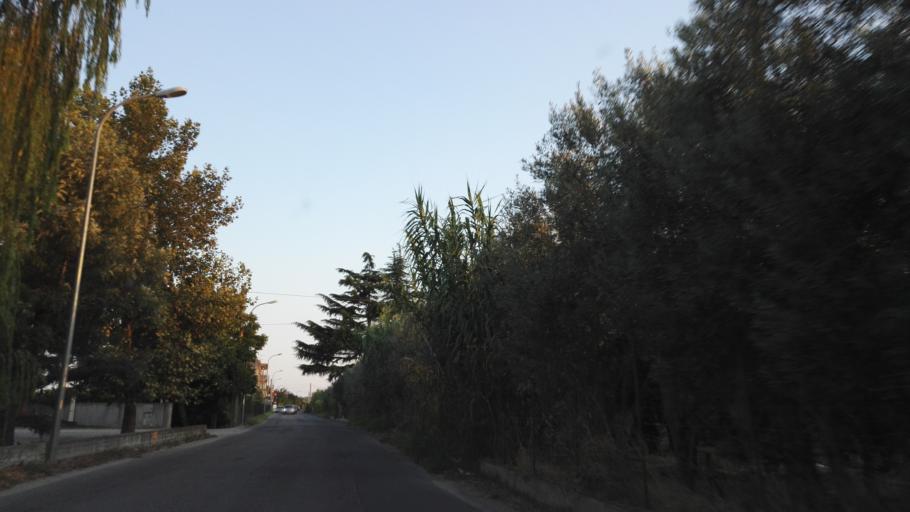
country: IT
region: Calabria
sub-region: Provincia di Reggio Calabria
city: Caulonia Marina
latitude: 38.3586
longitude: 16.4696
